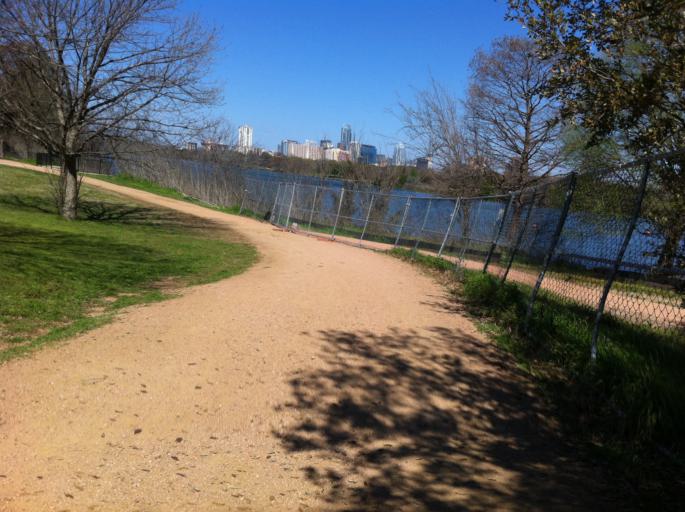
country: US
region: Texas
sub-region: Travis County
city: Austin
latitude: 30.2447
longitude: -97.7229
